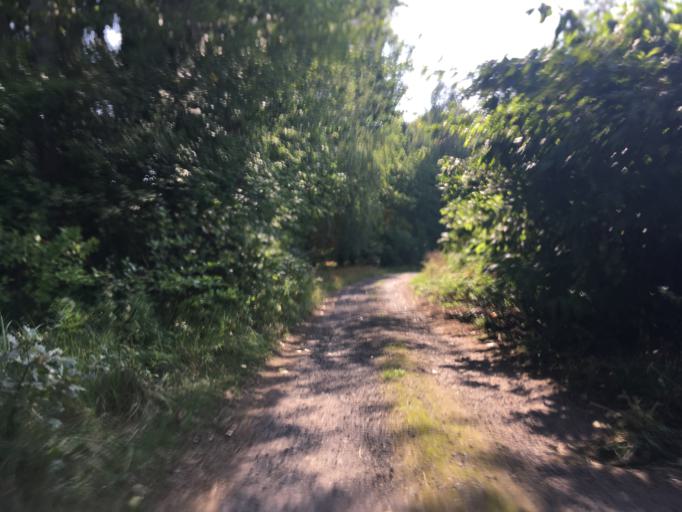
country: DE
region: Brandenburg
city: Erkner
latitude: 52.4033
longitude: 13.7304
